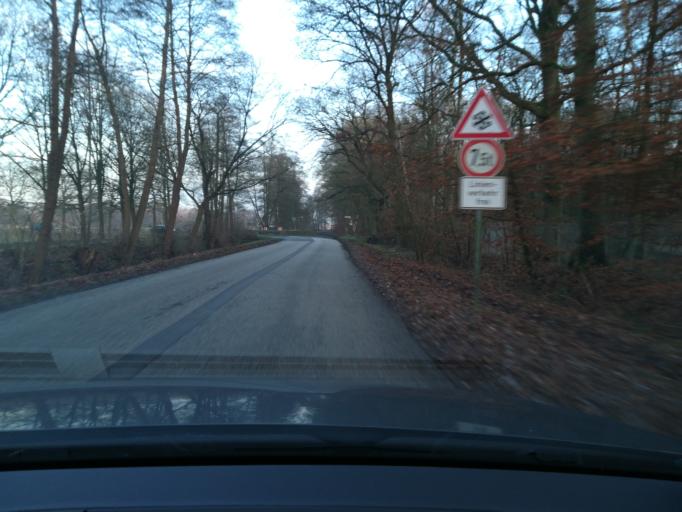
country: DE
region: Schleswig-Holstein
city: Escheburg
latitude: 53.4522
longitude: 10.3127
